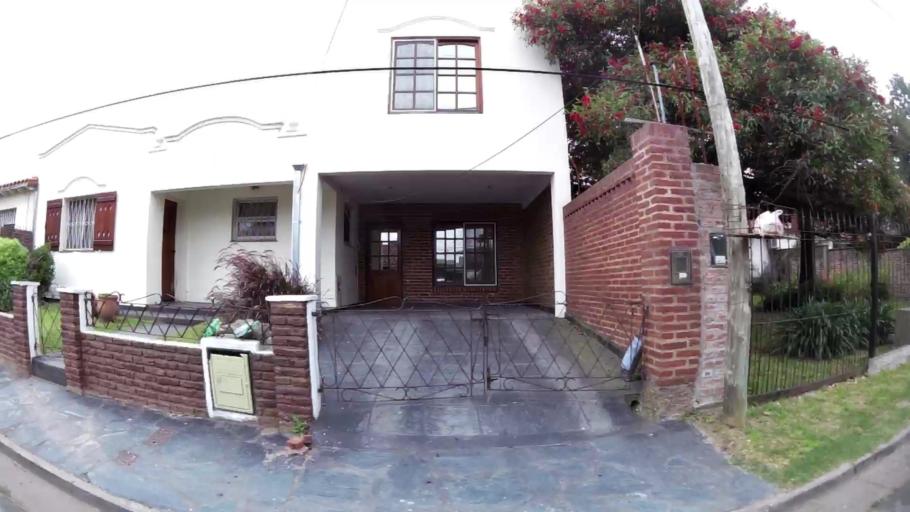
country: AR
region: Buenos Aires
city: San Justo
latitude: -34.7254
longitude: -58.5186
